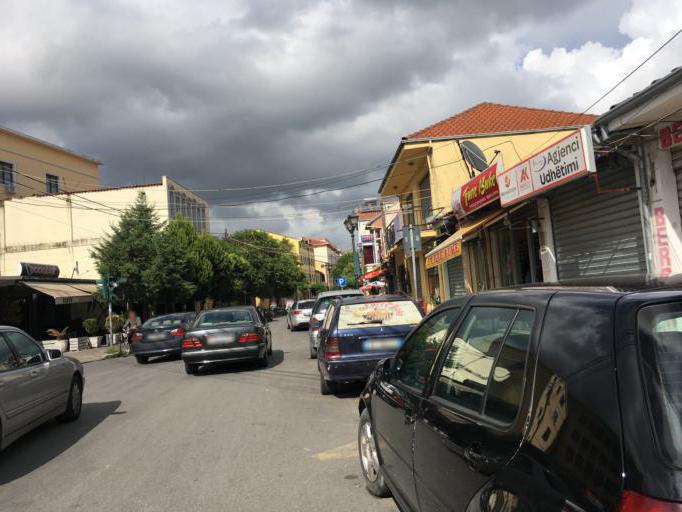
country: AL
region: Shkoder
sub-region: Rrethi i Shkodres
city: Shkoder
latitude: 42.0696
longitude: 19.5174
